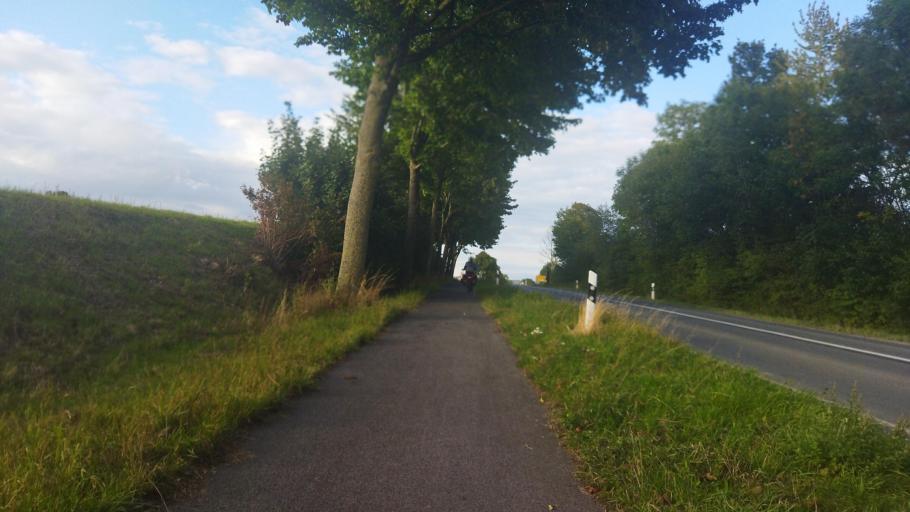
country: DE
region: North Rhine-Westphalia
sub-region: Regierungsbezirk Munster
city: Billerbeck
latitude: 51.9512
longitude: 7.2645
